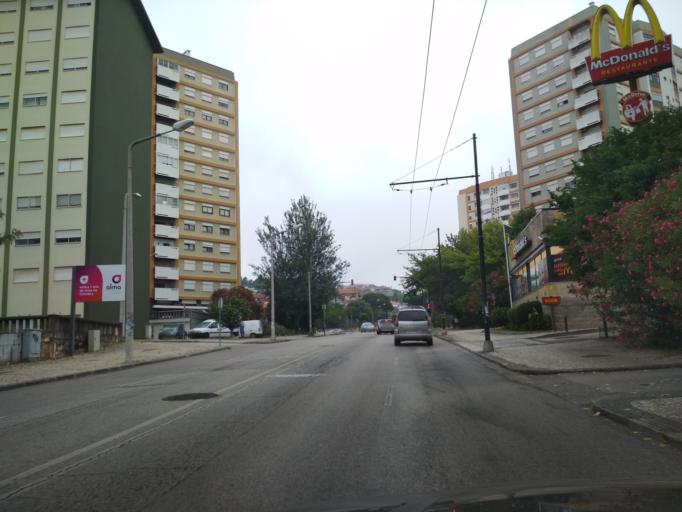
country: PT
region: Coimbra
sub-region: Coimbra
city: Coimbra
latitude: 40.2037
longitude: -8.4042
